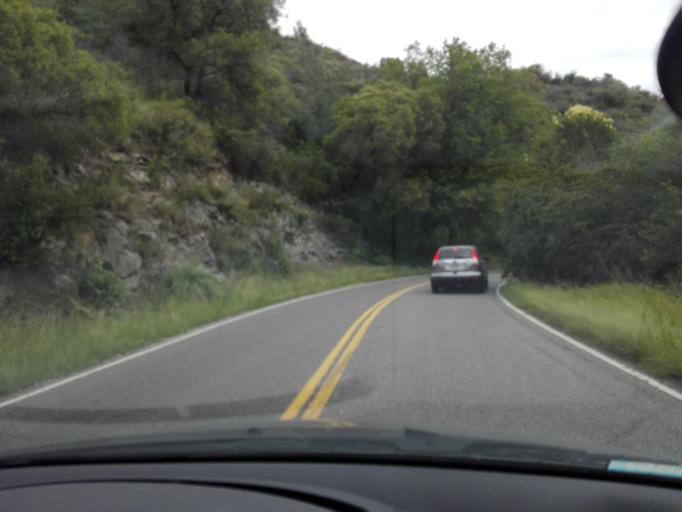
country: AR
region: Cordoba
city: Cuesta Blanca
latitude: -31.6041
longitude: -64.5522
